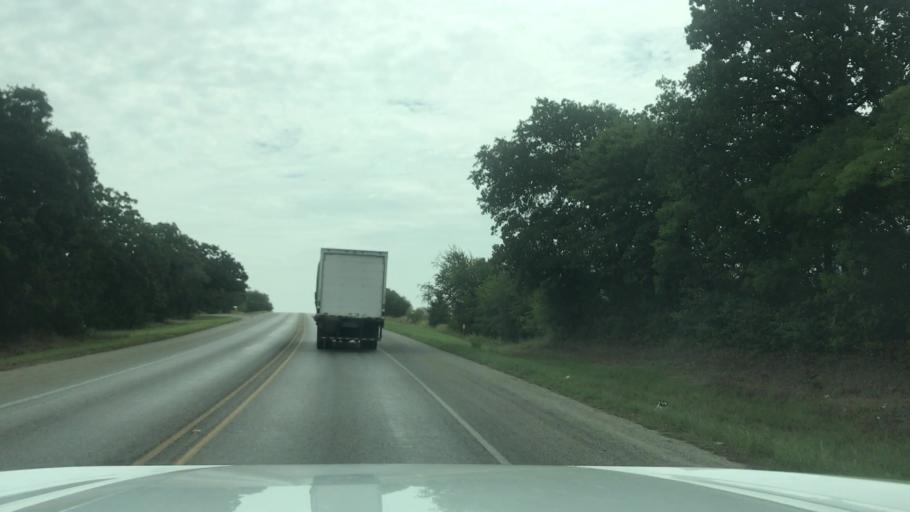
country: US
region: Texas
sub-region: Comanche County
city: De Leon
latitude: 32.1012
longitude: -98.4765
